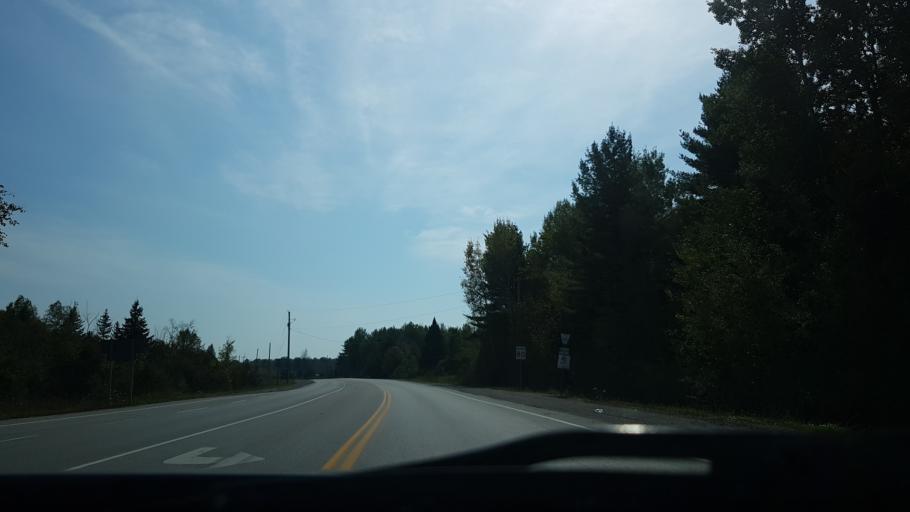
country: CA
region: Ontario
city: Orillia
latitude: 44.6594
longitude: -79.2567
